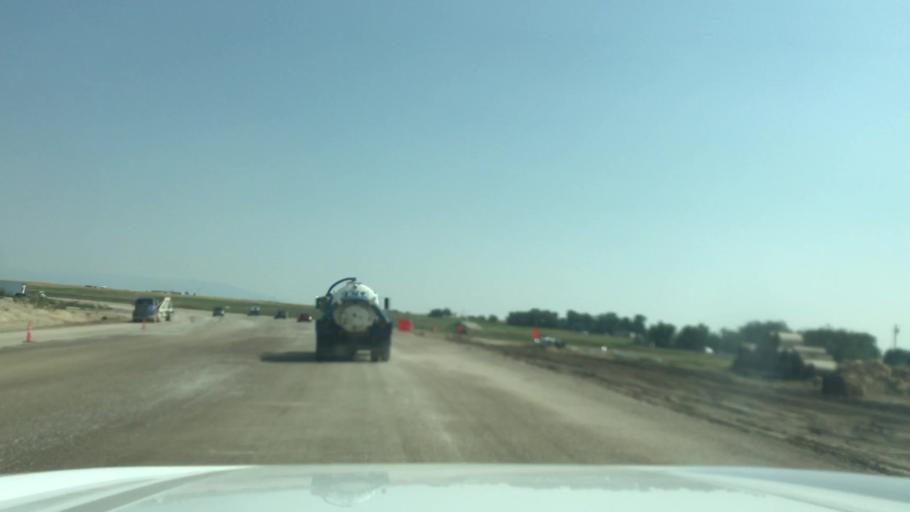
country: US
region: Montana
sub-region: Judith Basin County
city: Stanford
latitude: 47.0063
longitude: -109.8705
